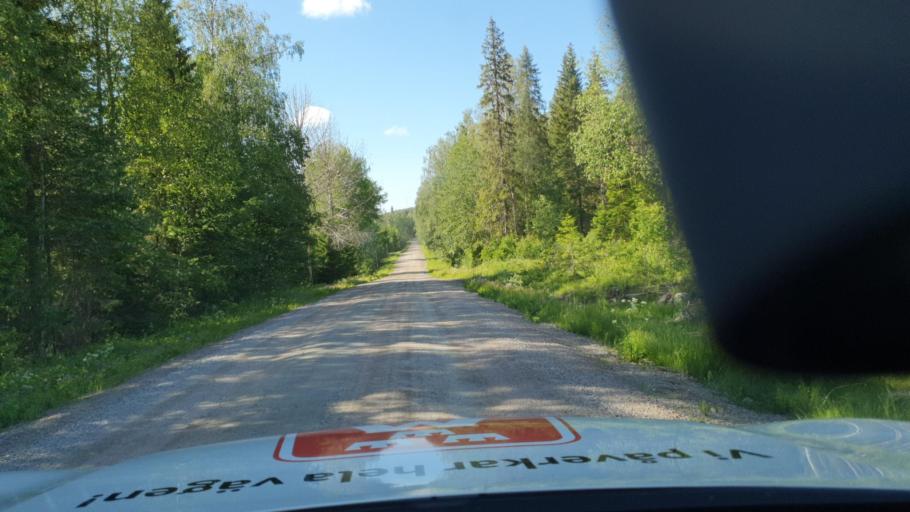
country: SE
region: Vaesterbotten
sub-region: Vannas Kommun
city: Vaennaes
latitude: 63.7815
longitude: 19.6331
